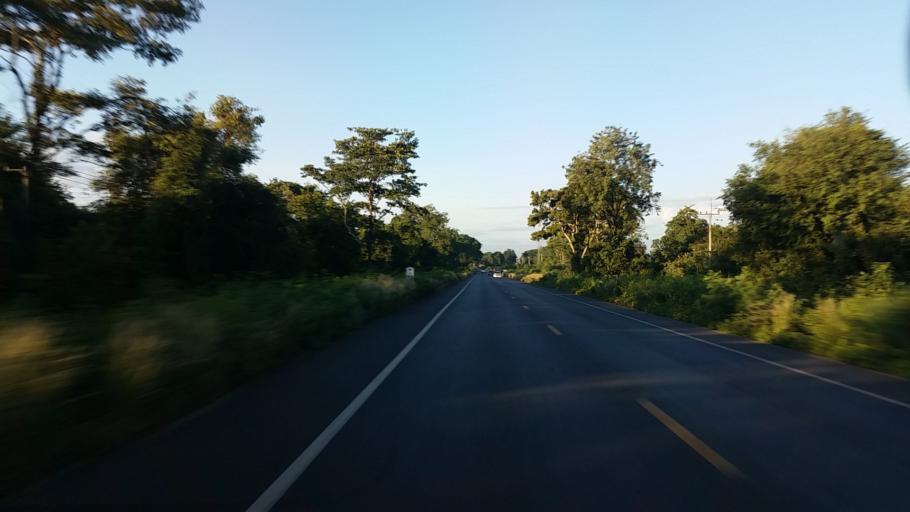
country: TH
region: Lop Buri
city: Chai Badan
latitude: 15.2600
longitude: 101.1857
